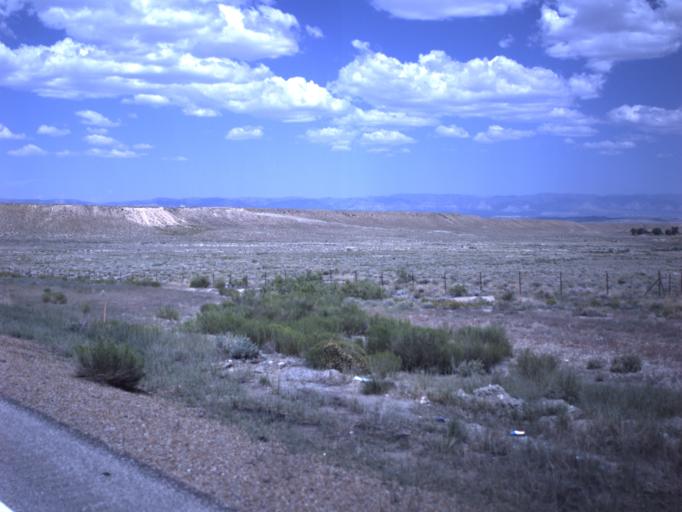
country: US
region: Utah
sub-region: Carbon County
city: Price
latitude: 39.4694
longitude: -110.8567
